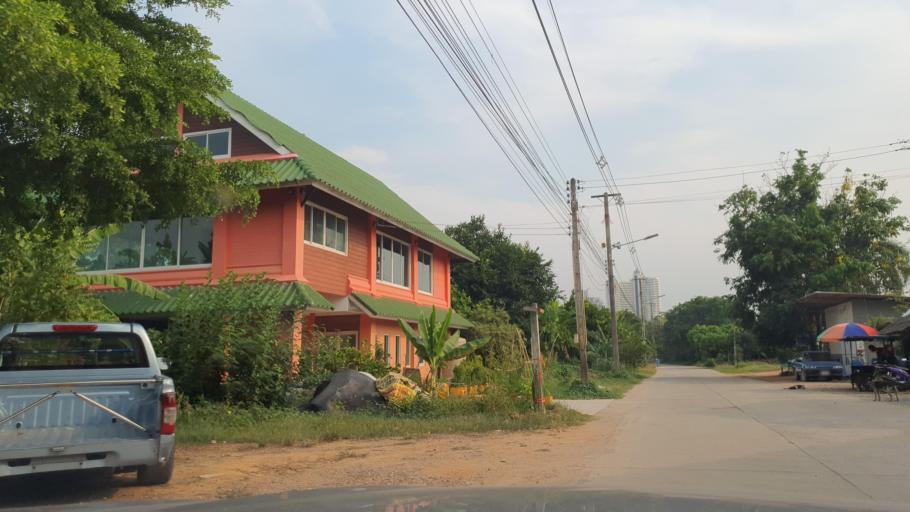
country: TH
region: Rayong
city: Rayong
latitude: 12.6123
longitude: 101.4011
